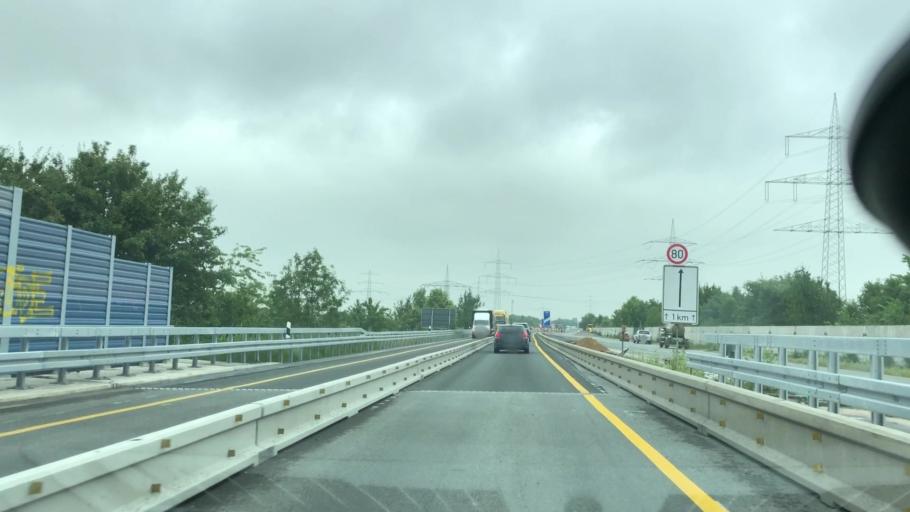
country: DE
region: North Rhine-Westphalia
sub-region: Regierungsbezirk Detmold
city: Paderborn
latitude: 51.6969
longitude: 8.7077
